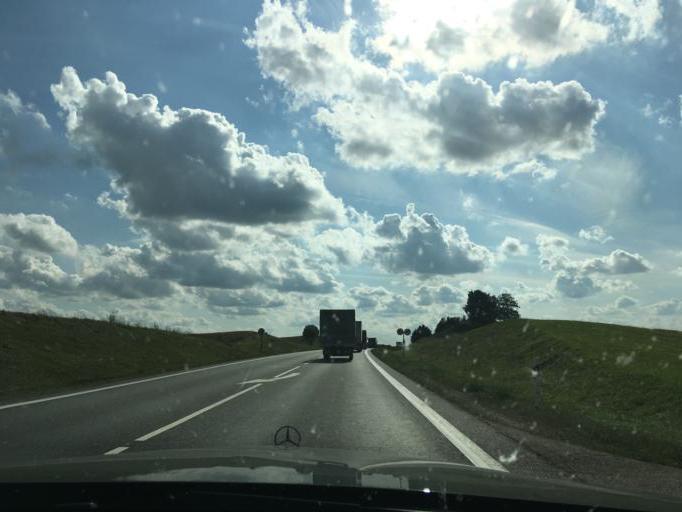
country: LT
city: Kalvarija
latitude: 54.4788
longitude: 23.2201
